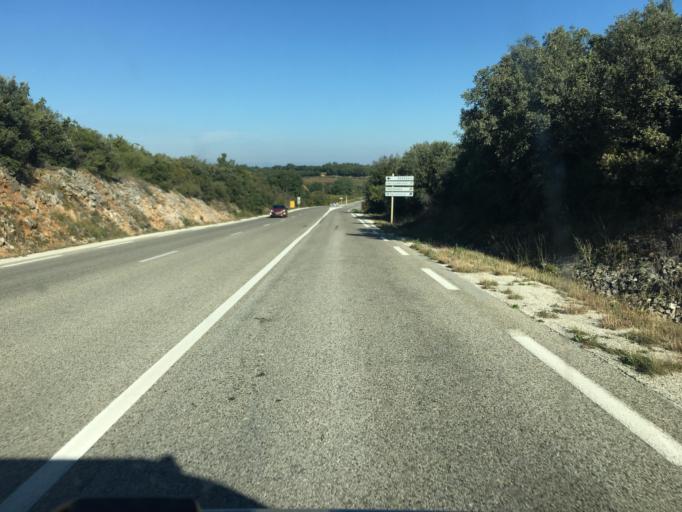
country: FR
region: Languedoc-Roussillon
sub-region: Departement du Gard
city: Sabran
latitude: 44.1331
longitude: 4.4753
